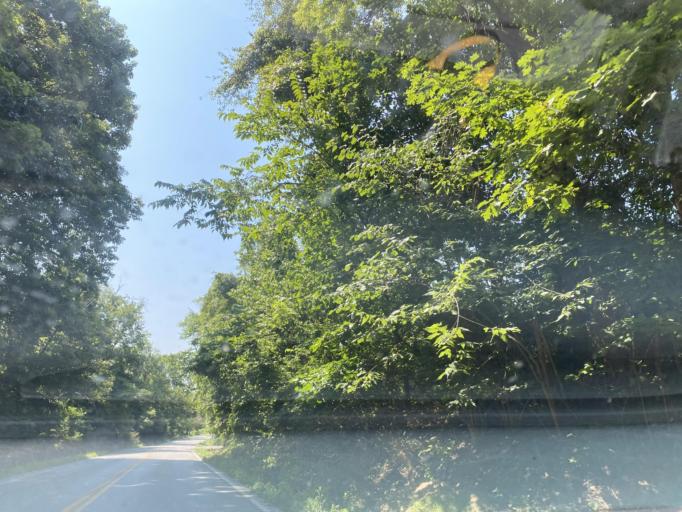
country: US
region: Kentucky
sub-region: Campbell County
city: Claryville
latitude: 38.9042
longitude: -84.4458
